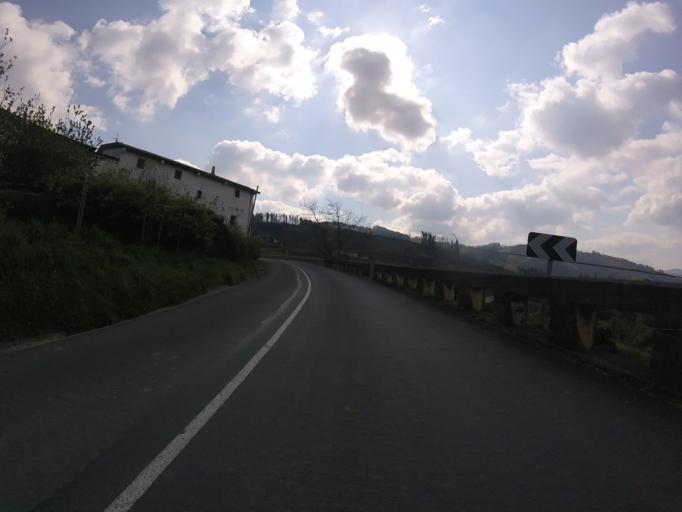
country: ES
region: Basque Country
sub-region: Provincia de Guipuzcoa
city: Azpeitia
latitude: 43.1657
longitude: -2.2292
